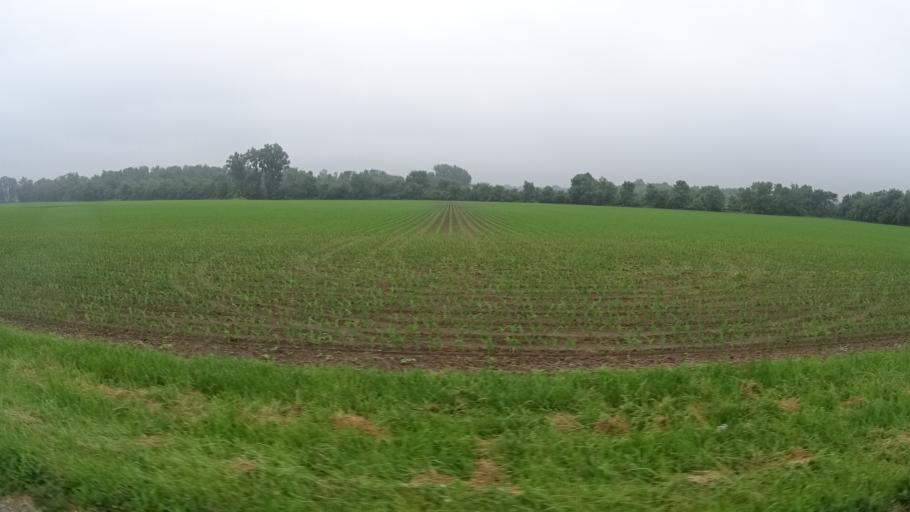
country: US
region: Ohio
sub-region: Huron County
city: Bellevue
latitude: 41.3622
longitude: -82.8087
